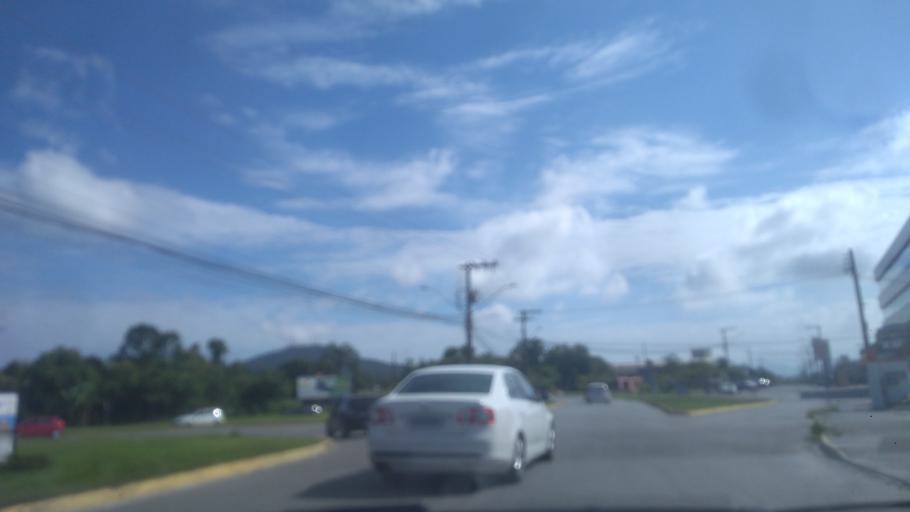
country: BR
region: Santa Catarina
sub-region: Joinville
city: Joinville
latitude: -26.3171
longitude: -48.8286
